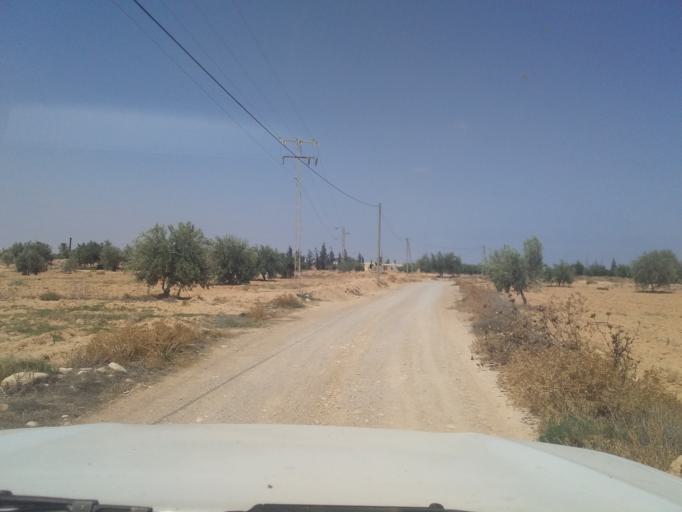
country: TN
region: Qabis
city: Matmata
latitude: 33.5970
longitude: 10.2822
